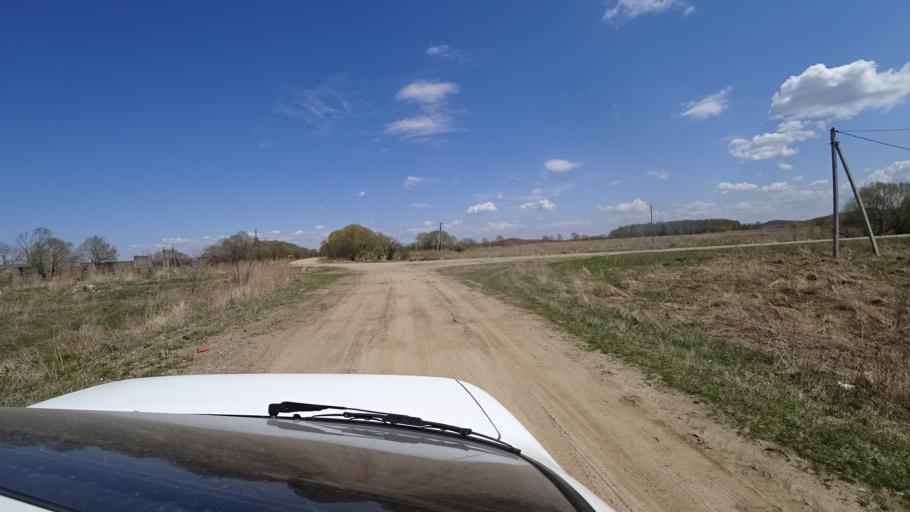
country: RU
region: Primorskiy
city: Dal'nerechensk
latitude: 45.8007
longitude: 133.7718
